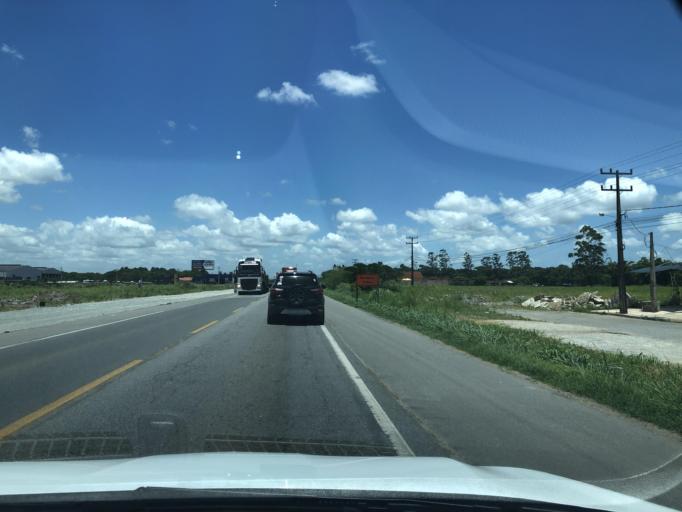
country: BR
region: Santa Catarina
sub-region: Joinville
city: Joinville
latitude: -26.3870
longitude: -48.7309
